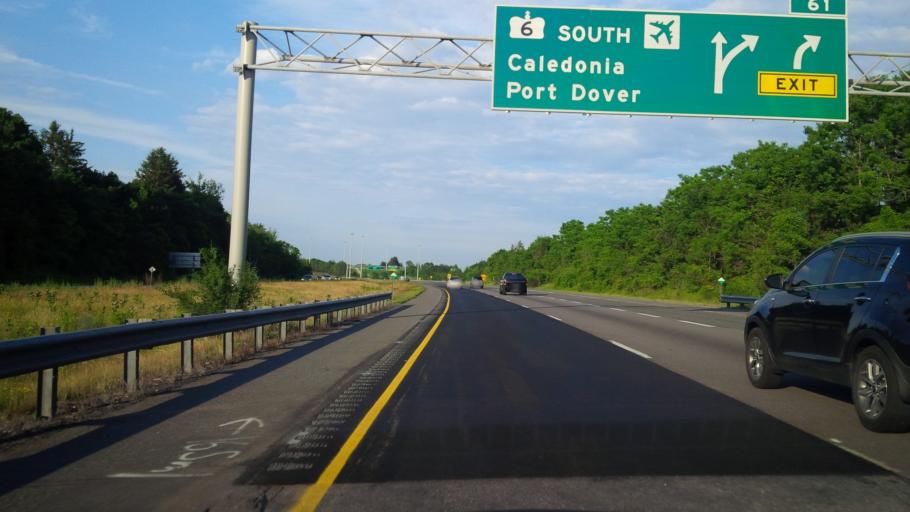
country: CA
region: Ontario
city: Ancaster
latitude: 43.2058
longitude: -79.9805
